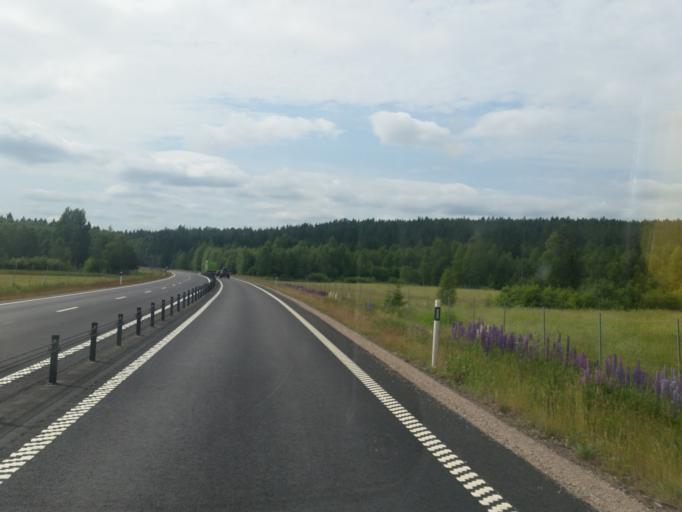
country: SE
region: Dalarna
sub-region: Borlange Kommun
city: Borlaenge
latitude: 60.4574
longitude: 15.3742
